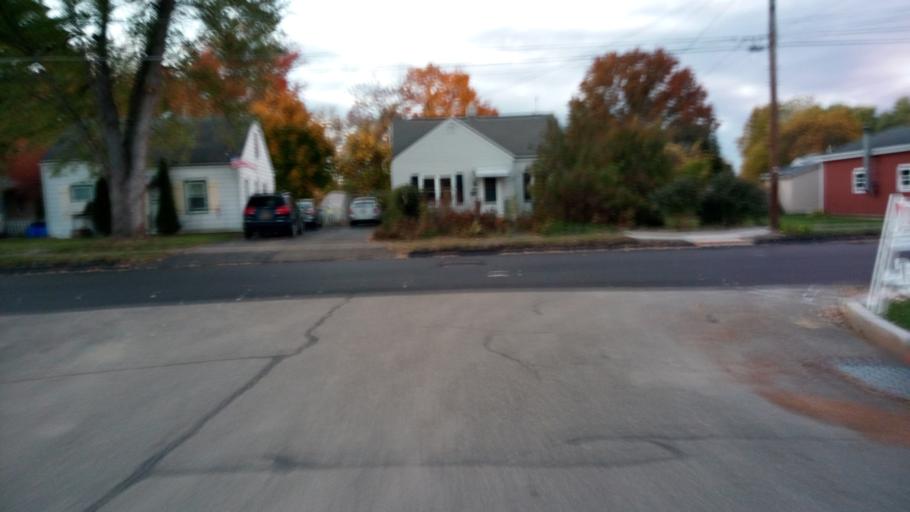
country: US
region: New York
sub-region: Chemung County
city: Elmira
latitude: 42.0791
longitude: -76.8161
